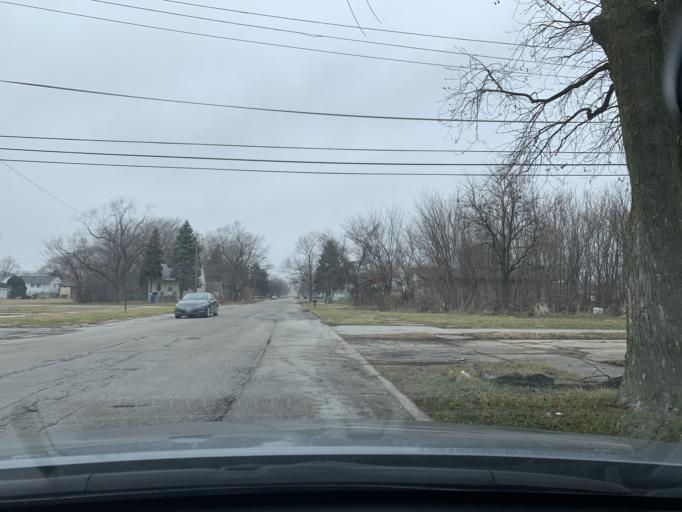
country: US
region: Illinois
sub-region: Cook County
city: Dixmoor
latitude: 41.6229
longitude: -87.6705
